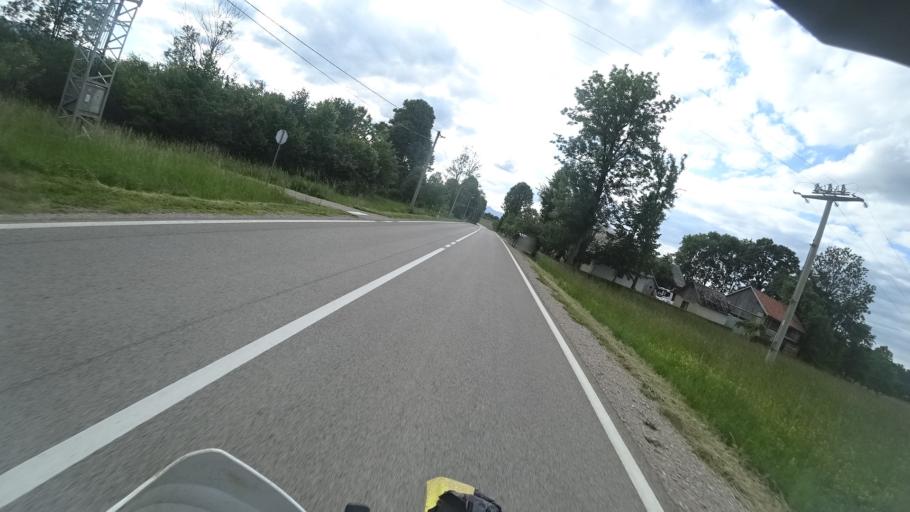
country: HR
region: Licko-Senjska
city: Gospic
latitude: 44.5093
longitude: 15.4359
